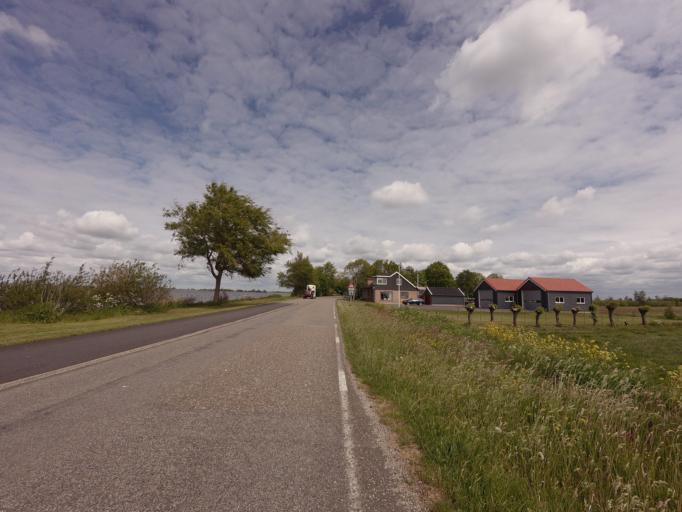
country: NL
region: Friesland
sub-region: Gemeente Gaasterlan-Sleat
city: Balk
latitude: 52.9374
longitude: 5.5585
